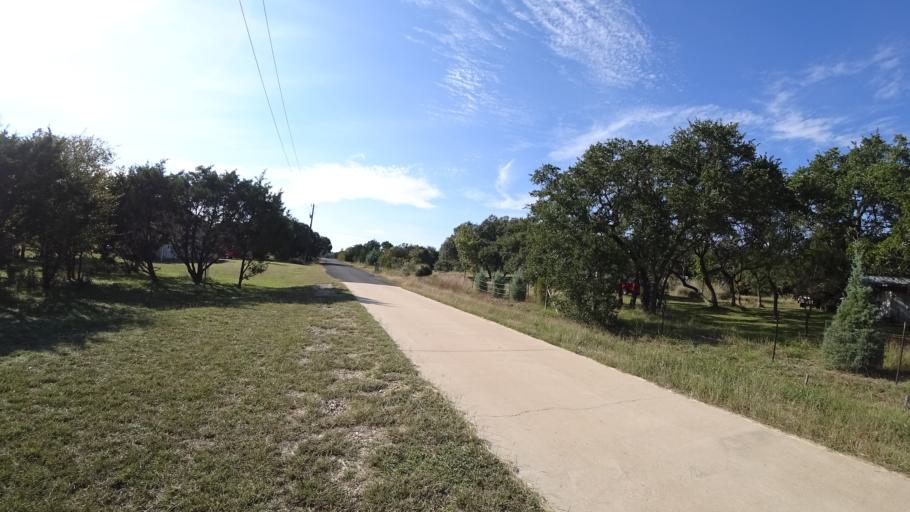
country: US
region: Texas
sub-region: Travis County
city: Bee Cave
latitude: 30.2379
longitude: -97.9335
